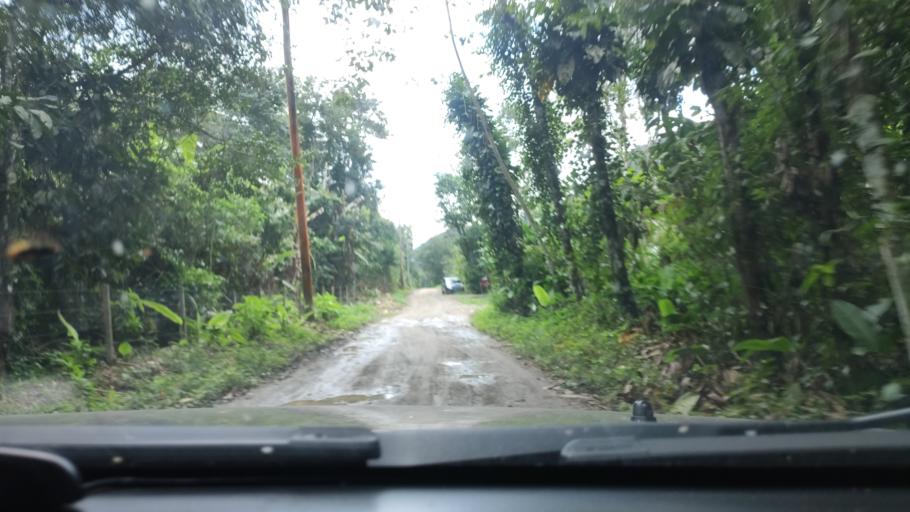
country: BR
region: Sao Paulo
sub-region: Sao Sebastiao
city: Sao Sebastiao
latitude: -23.7291
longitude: -45.4928
